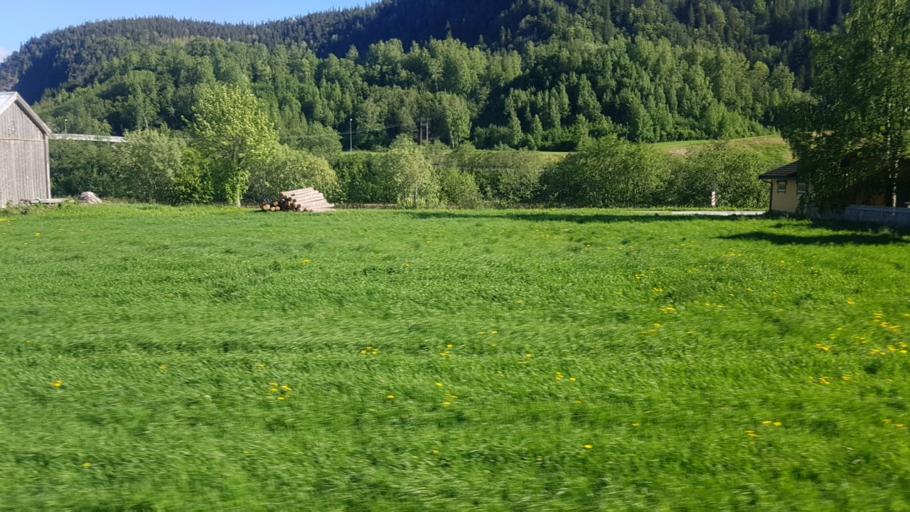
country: NO
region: Sor-Trondelag
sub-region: Midtre Gauldal
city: Storen
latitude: 63.0788
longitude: 10.2604
